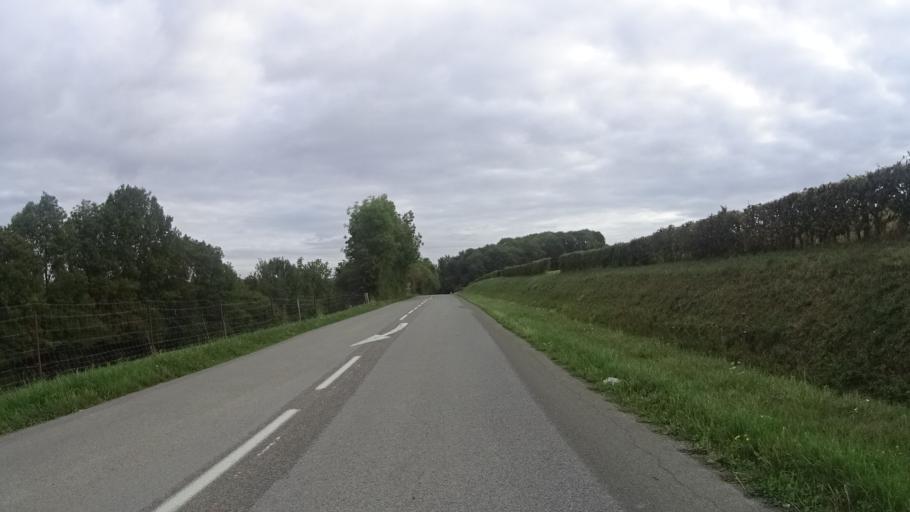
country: FR
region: Picardie
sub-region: Departement de l'Aisne
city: Guise
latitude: 49.9188
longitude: 3.5781
